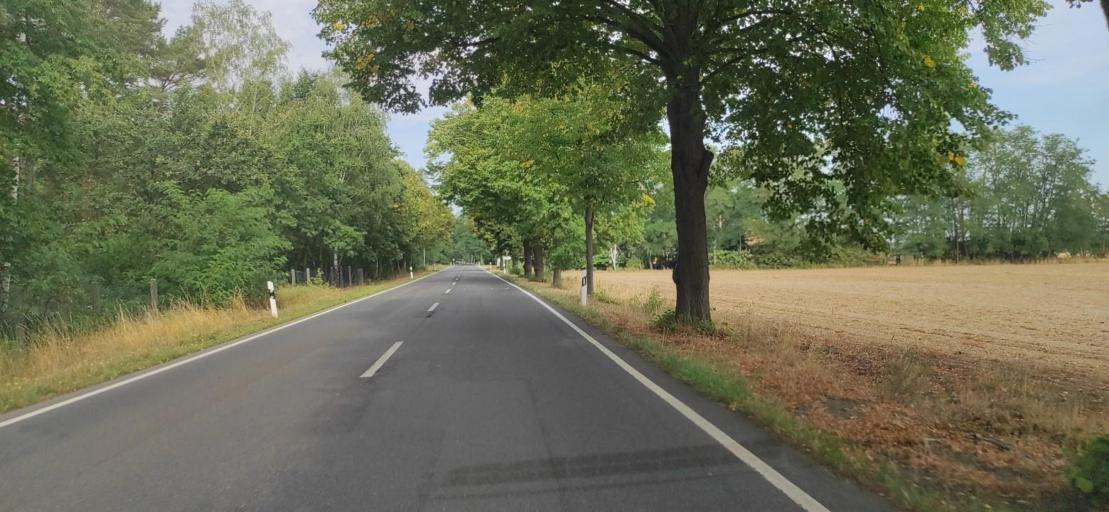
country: DE
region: Brandenburg
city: Forst
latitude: 51.7050
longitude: 14.6844
